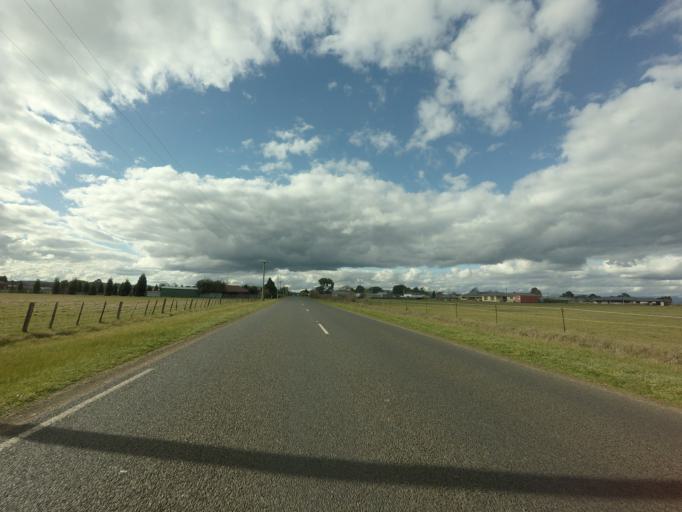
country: AU
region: Tasmania
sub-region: Northern Midlands
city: Longford
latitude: -41.6116
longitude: 147.1144
